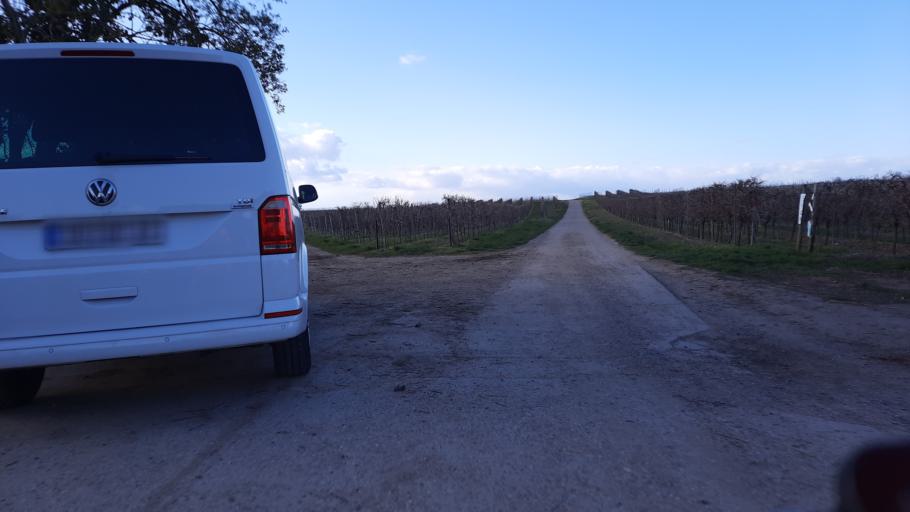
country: DE
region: Rheinland-Pfalz
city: Offstein
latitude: 49.6090
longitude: 8.2627
